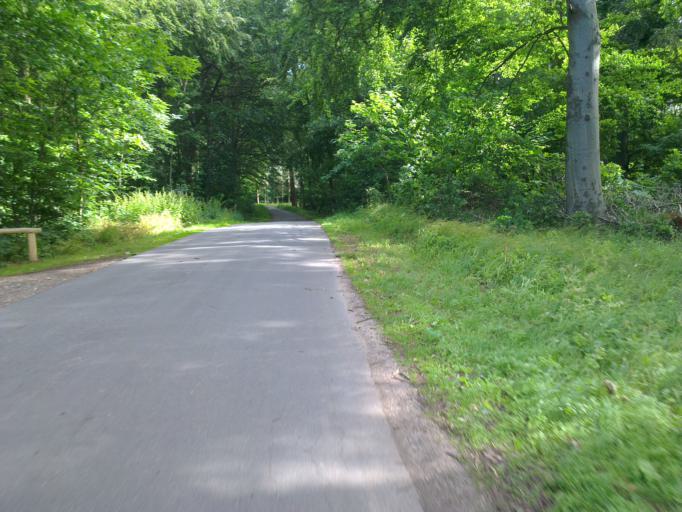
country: DK
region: Capital Region
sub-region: Frederikssund Kommune
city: Jaegerspris
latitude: 55.8738
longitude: 11.9845
